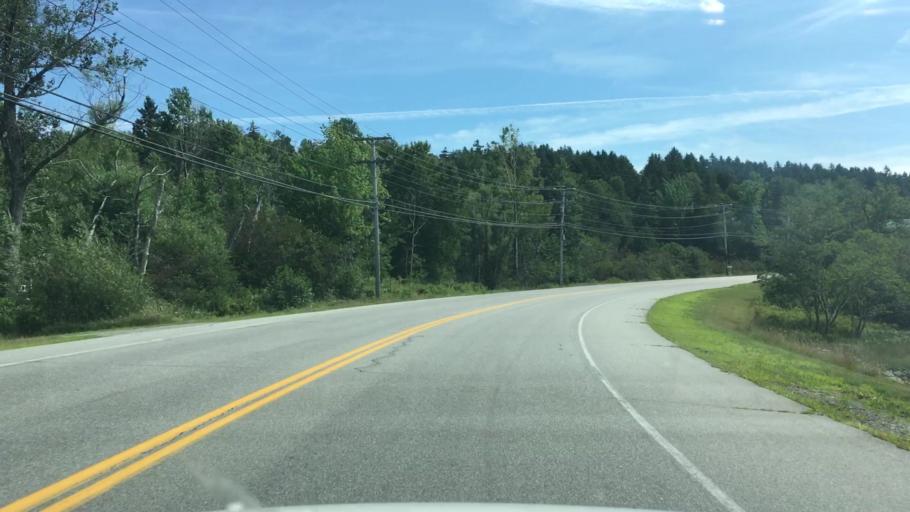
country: US
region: Maine
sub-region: Washington County
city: Eastport
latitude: 44.9235
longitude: -67.0150
